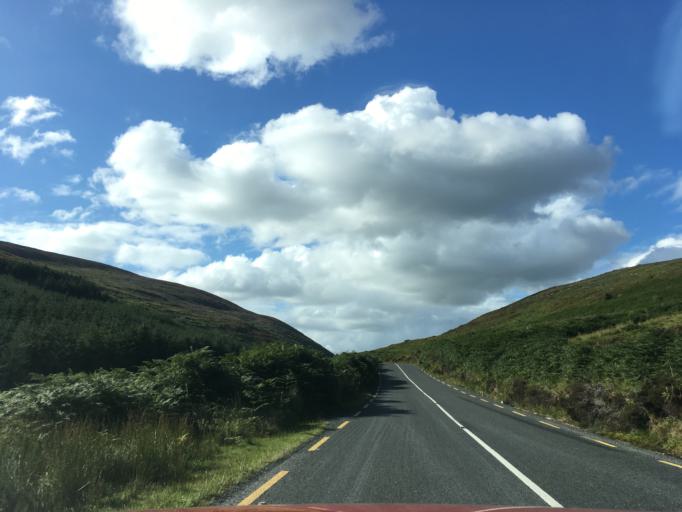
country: IE
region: Munster
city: Cahir
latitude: 52.2355
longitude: -7.9518
